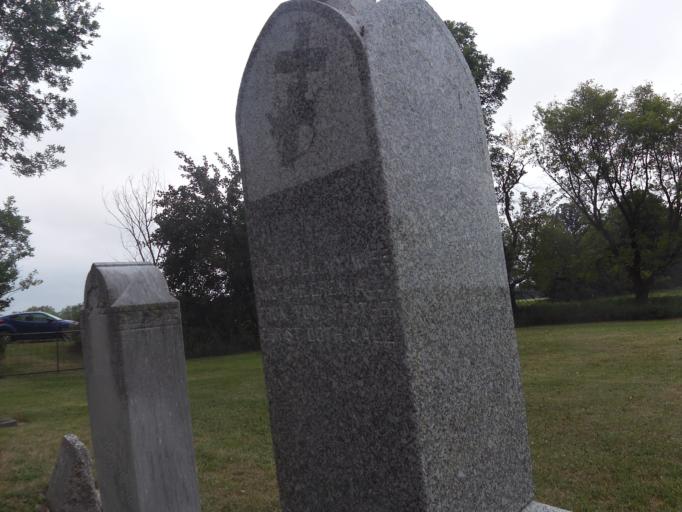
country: US
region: North Dakota
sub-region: Walsh County
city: Grafton
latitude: 48.4281
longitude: -97.1292
